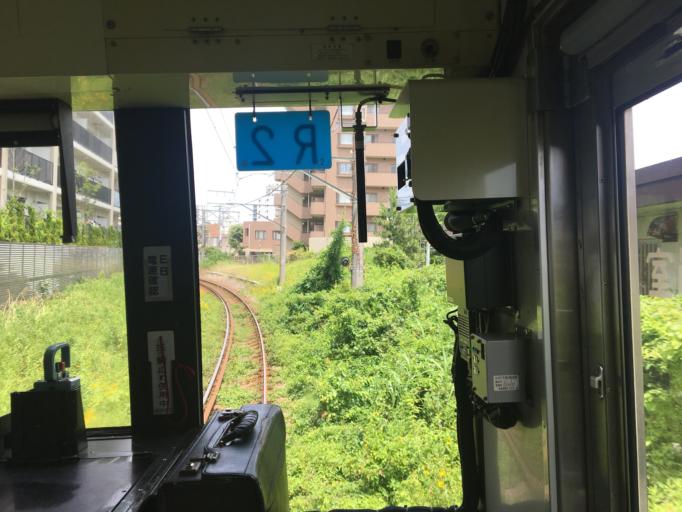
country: JP
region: Kanagawa
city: Chigasaki
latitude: 35.3324
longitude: 139.4107
